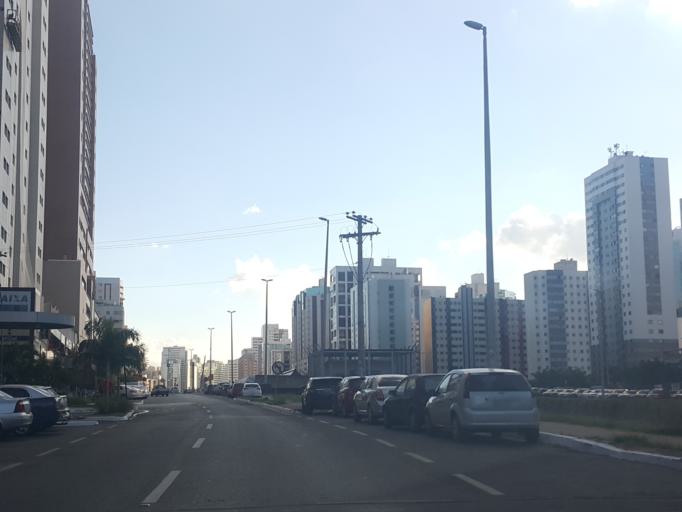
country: BR
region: Federal District
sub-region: Brasilia
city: Brasilia
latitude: -15.8361
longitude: -48.0150
